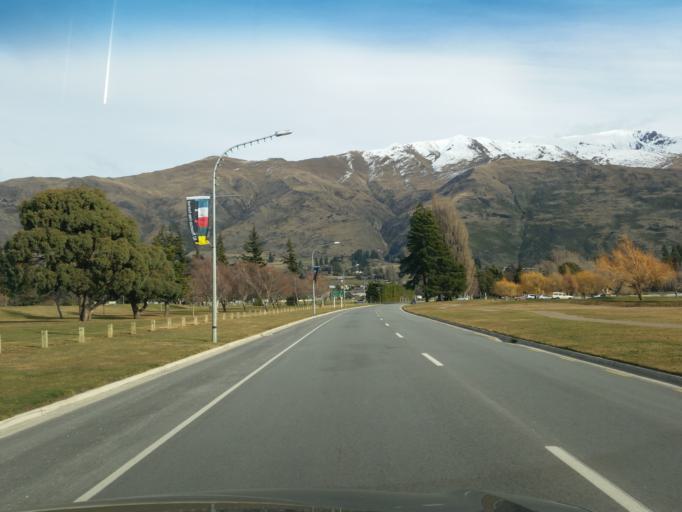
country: NZ
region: Otago
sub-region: Queenstown-Lakes District
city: Wanaka
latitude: -44.6975
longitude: 169.1304
